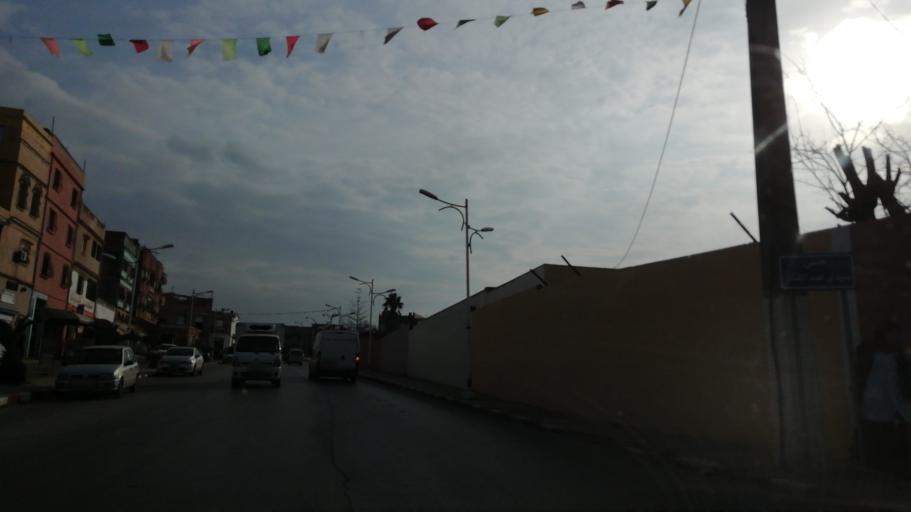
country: DZ
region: Mostaganem
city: Mostaganem
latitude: 35.8985
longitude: 0.0739
